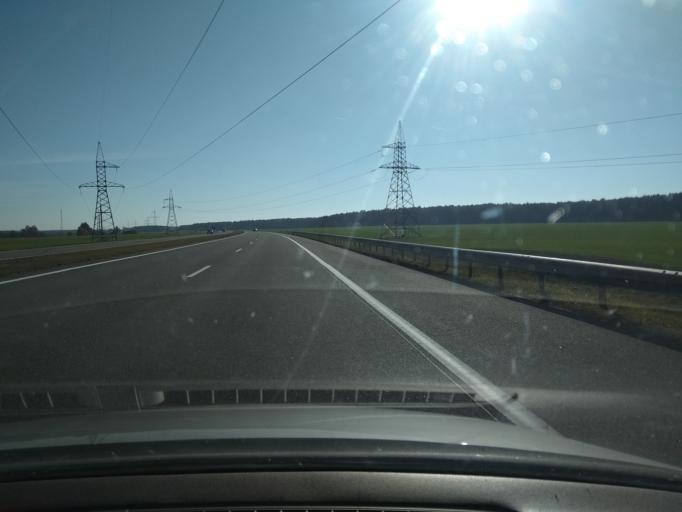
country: BY
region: Brest
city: Baranovichi
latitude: 53.1029
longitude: 25.8875
